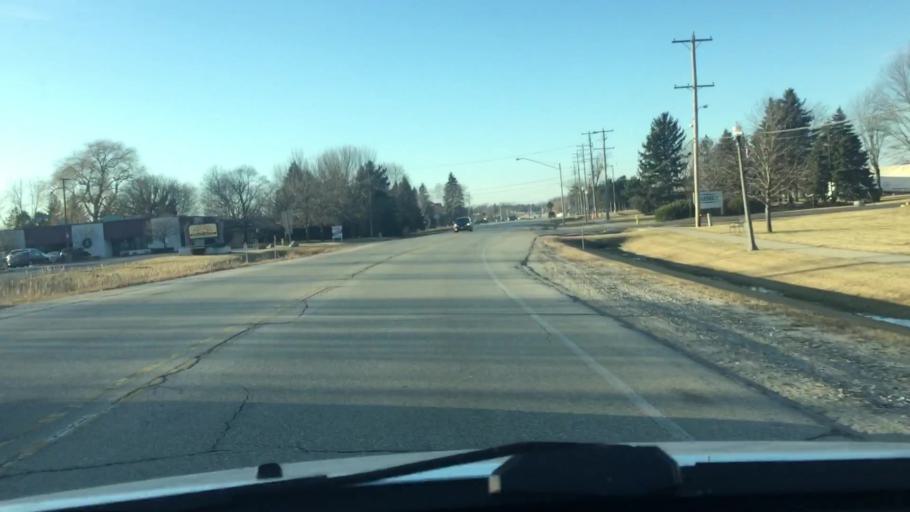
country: US
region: Wisconsin
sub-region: Waukesha County
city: Sussex
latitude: 43.1345
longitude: -88.2384
